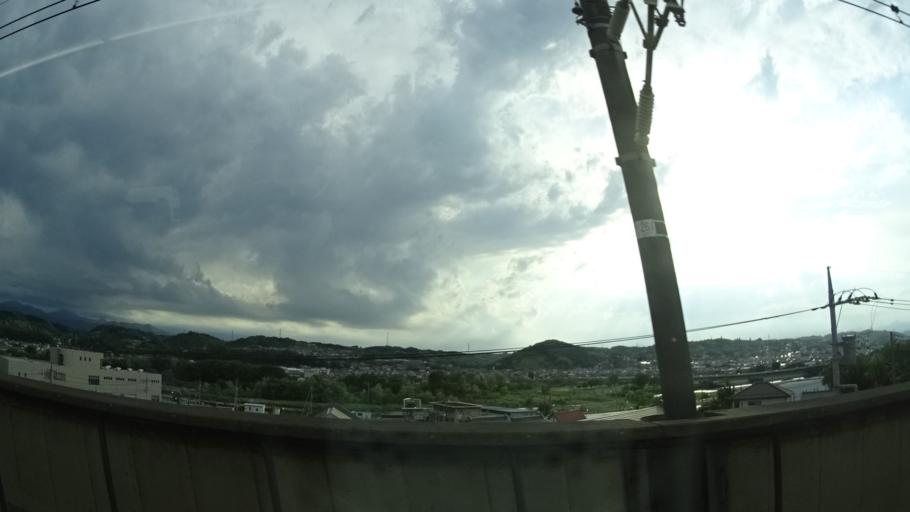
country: JP
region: Gunma
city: Takasaki
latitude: 36.3085
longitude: 139.0157
